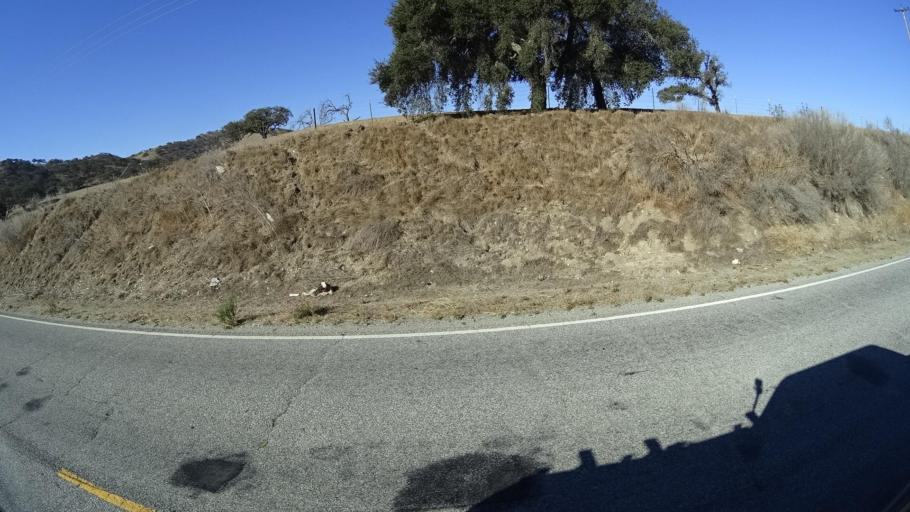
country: US
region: California
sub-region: Monterey County
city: King City
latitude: 36.1576
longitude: -121.1327
